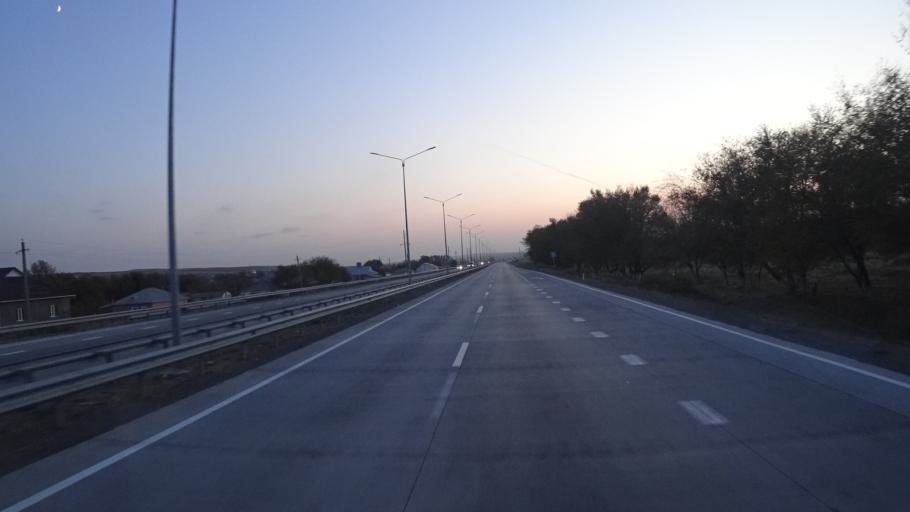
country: KZ
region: Ongtustik Qazaqstan
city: Qazyqurt
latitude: 41.8837
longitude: 69.4399
